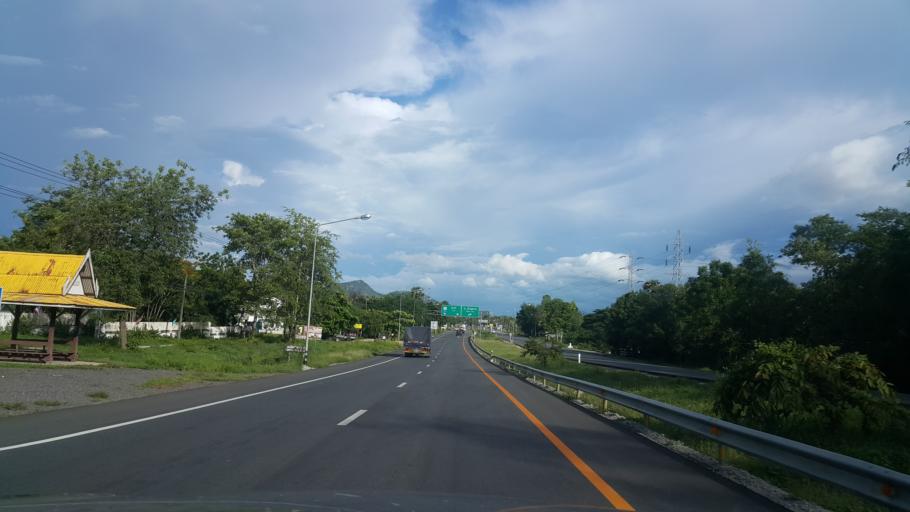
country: TH
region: Tak
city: Ban Tak
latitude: 17.0382
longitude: 99.0857
